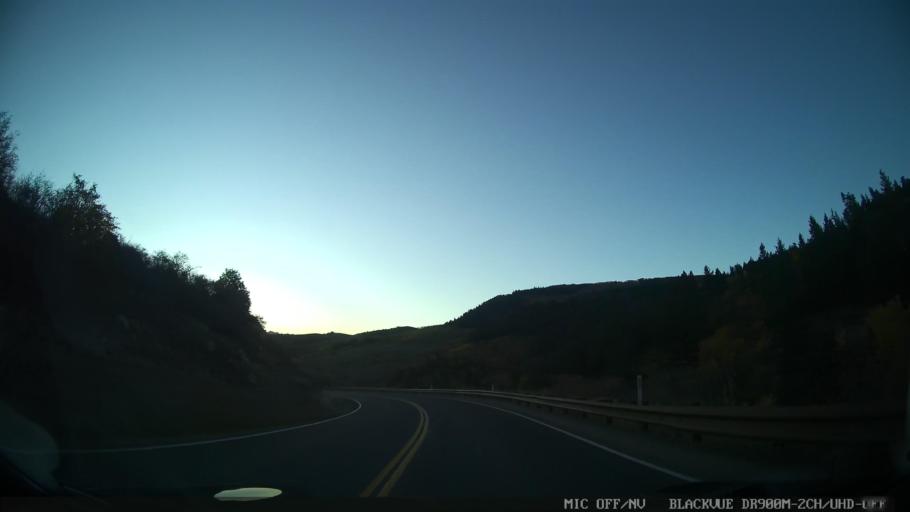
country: US
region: Colorado
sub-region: Eagle County
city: Edwards
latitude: 39.8158
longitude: -106.6684
